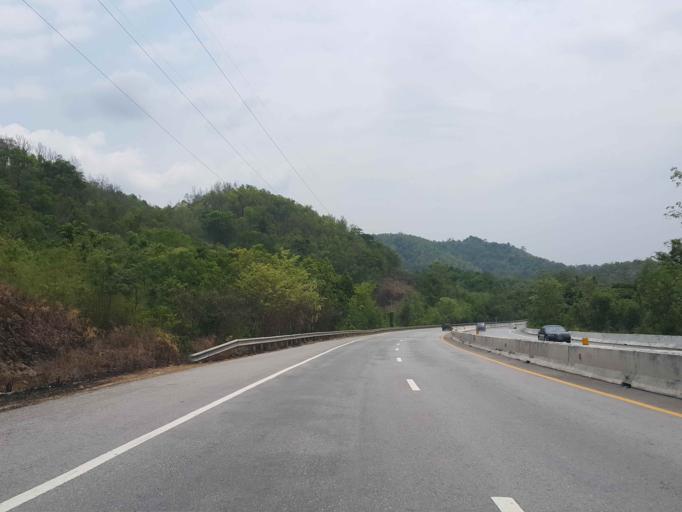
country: TH
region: Lampang
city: Sop Prap
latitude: 17.8401
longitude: 99.2934
